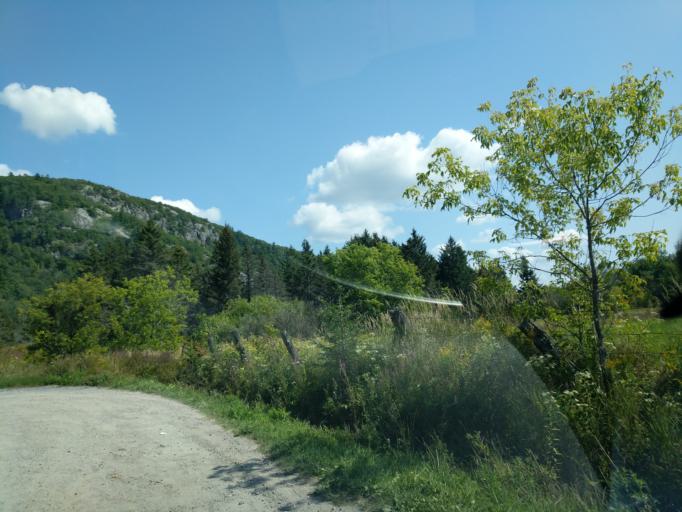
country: CA
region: Quebec
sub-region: Outaouais
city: Wakefield
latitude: 45.5303
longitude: -75.9869
